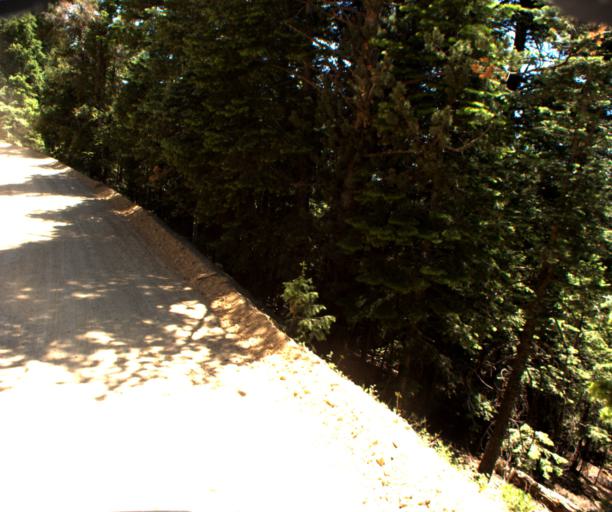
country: US
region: Arizona
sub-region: Graham County
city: Swift Trail Junction
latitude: 32.6617
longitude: -109.8662
